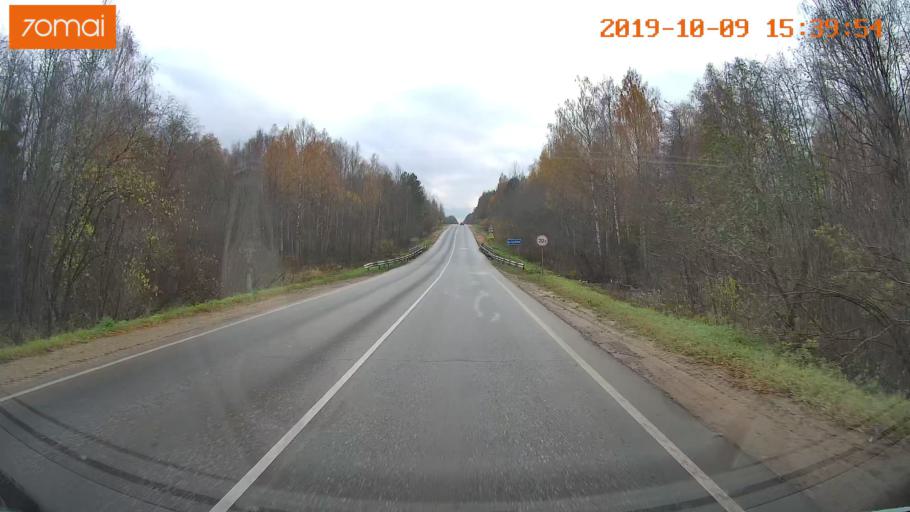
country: RU
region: Kostroma
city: Oktyabr'skiy
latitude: 57.8927
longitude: 41.1552
